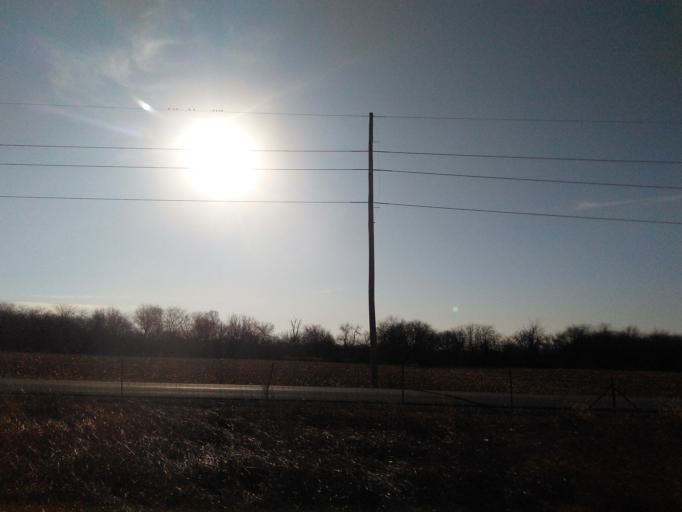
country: US
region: Illinois
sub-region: Madison County
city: Highland
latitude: 38.8087
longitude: -89.5820
